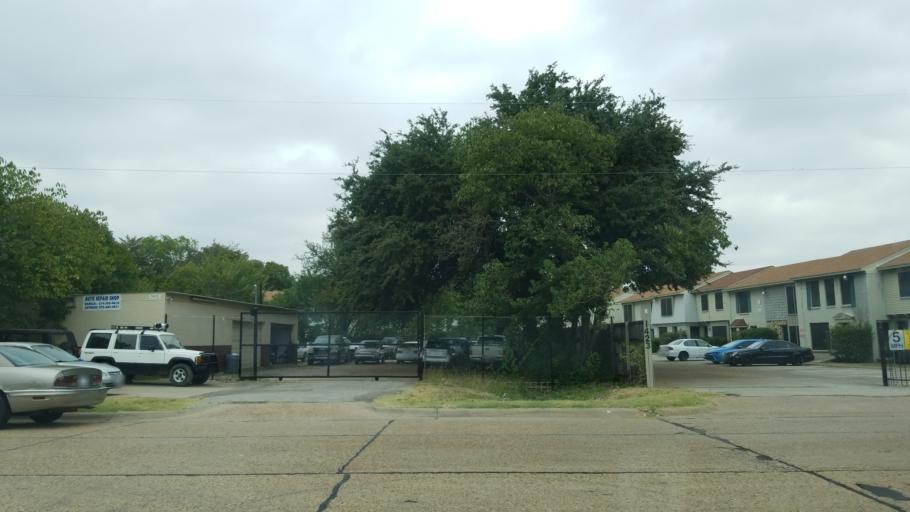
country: US
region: Texas
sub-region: Dallas County
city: Garland
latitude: 32.9094
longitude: -96.6510
